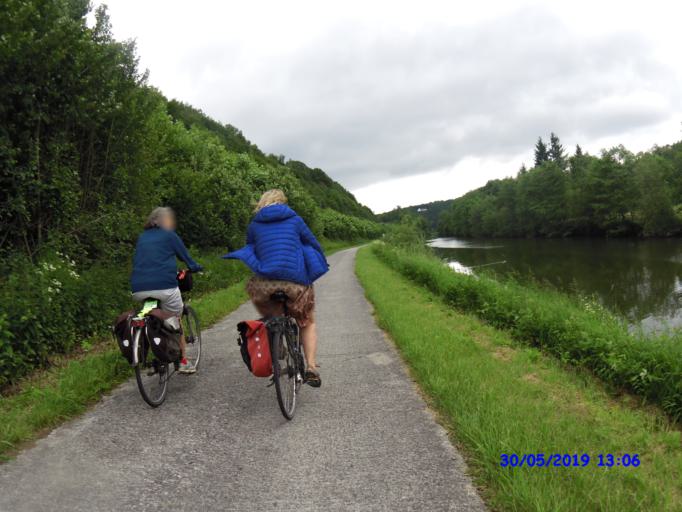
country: BE
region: Wallonia
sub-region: Province du Hainaut
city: Thuin
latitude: 50.3525
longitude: 4.3085
